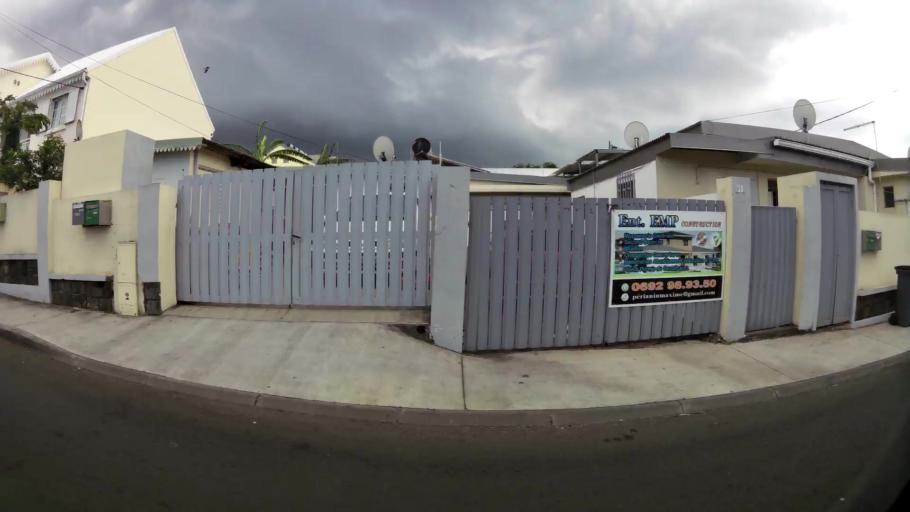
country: RE
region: Reunion
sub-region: Reunion
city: Saint-Denis
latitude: -20.8889
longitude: 55.4742
